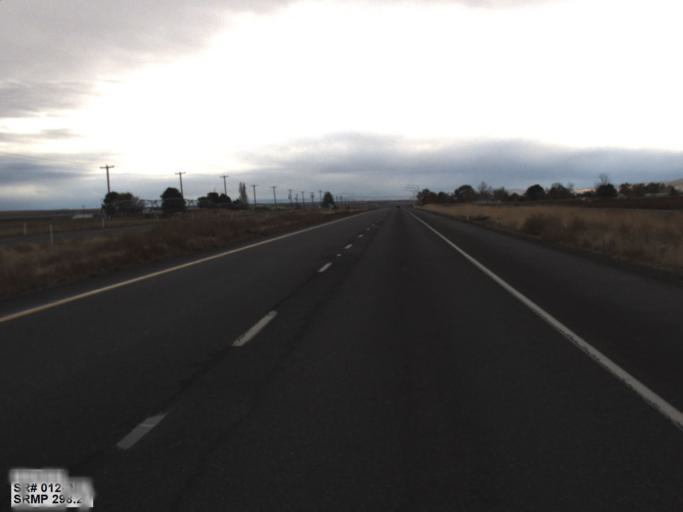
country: US
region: Washington
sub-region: Walla Walla County
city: Burbank
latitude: 46.1796
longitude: -118.9706
